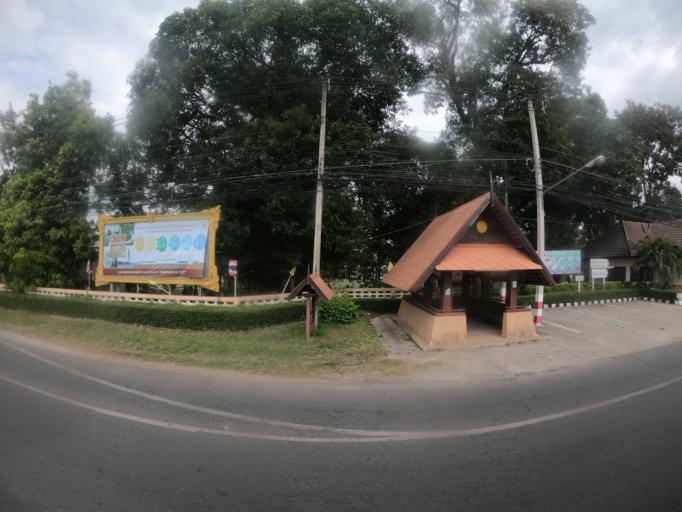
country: TH
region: Maha Sarakham
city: Maha Sarakham
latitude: 16.2025
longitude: 103.2900
